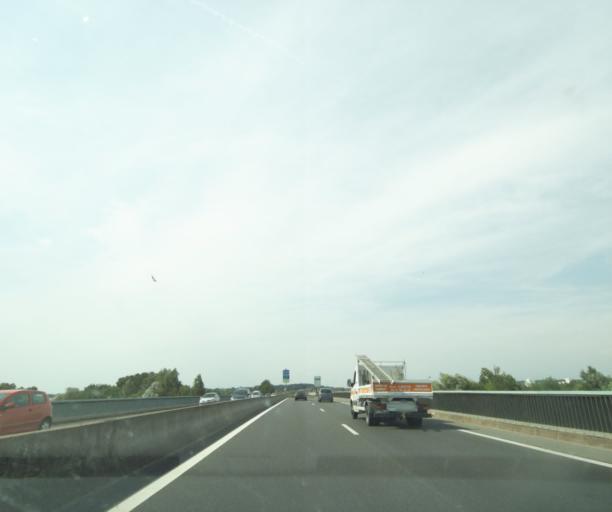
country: FR
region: Centre
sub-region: Departement d'Indre-et-Loire
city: La Riche
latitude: 47.3741
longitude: 0.6526
